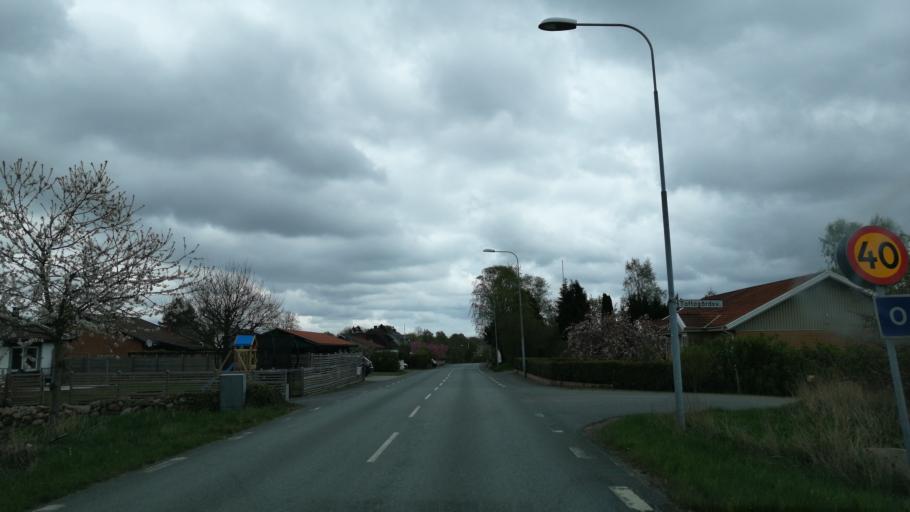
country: SE
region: Skane
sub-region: Kristianstads Kommun
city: Onnestad
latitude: 55.9931
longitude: 14.0306
